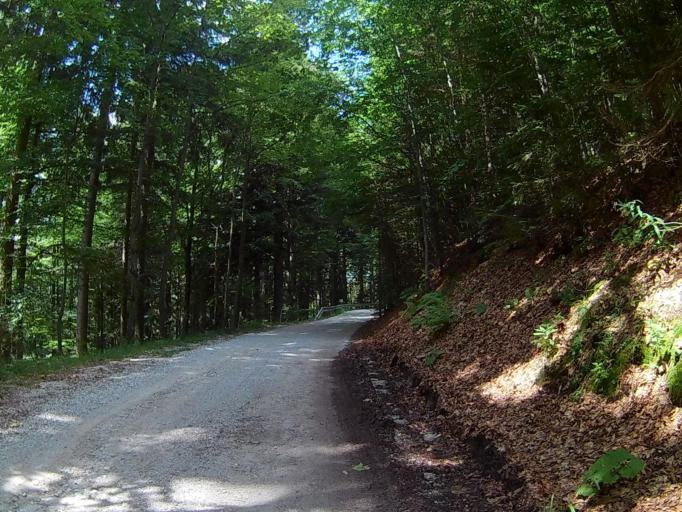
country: SI
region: Selnica ob Dravi
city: Selnica ob Dravi
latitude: 46.4859
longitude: 15.4580
